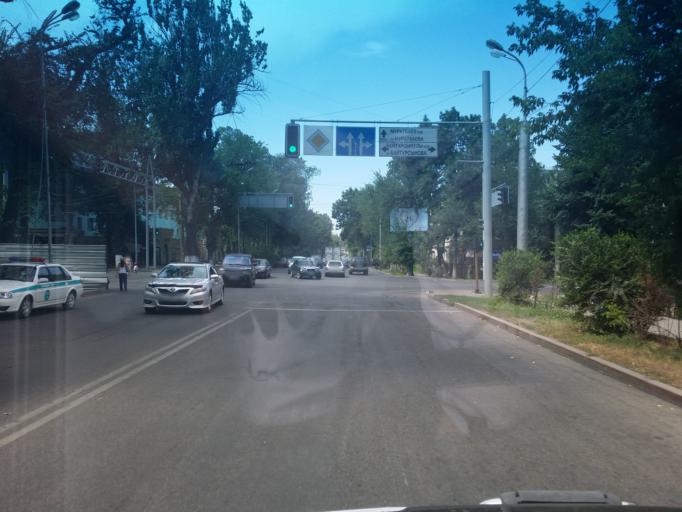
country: KZ
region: Almaty Qalasy
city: Almaty
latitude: 43.2434
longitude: 76.9278
